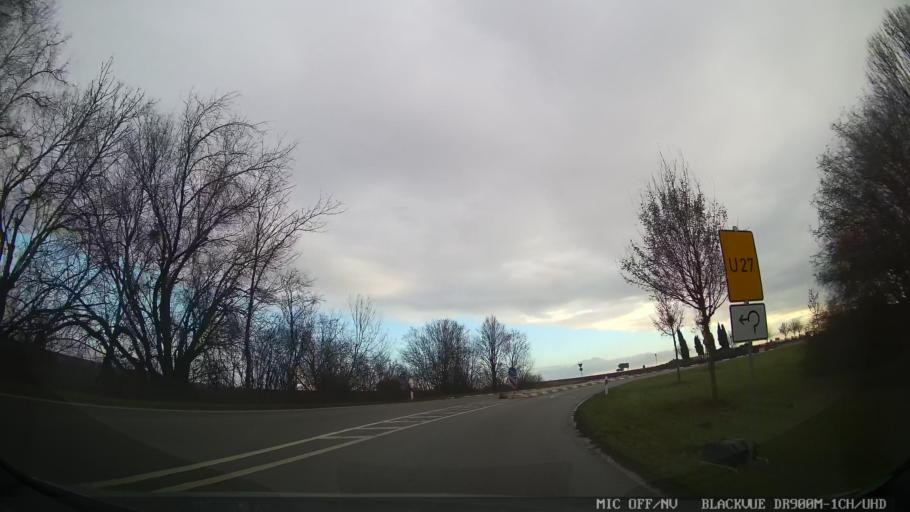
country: DE
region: Rheinland-Pfalz
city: Friesenheim
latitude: 49.8429
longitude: 8.2550
